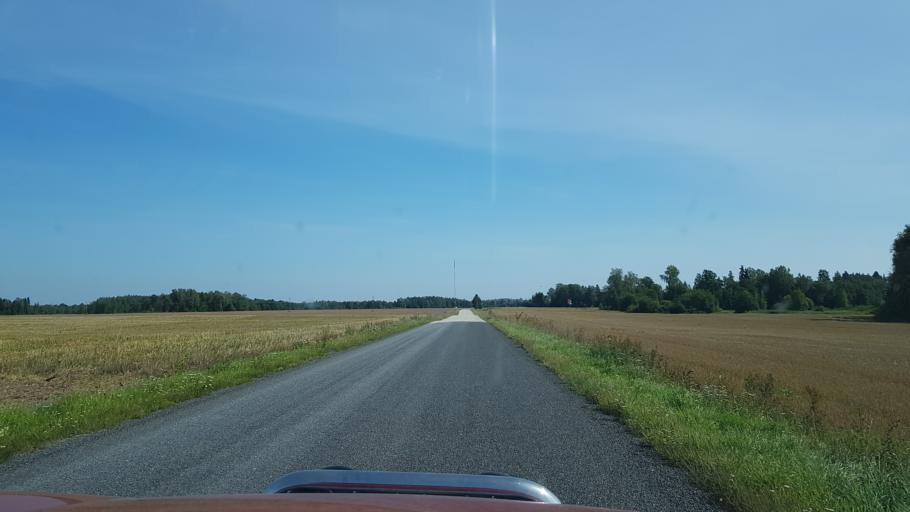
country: EE
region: Viljandimaa
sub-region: Viljandi linn
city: Viljandi
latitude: 58.4877
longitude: 25.6118
